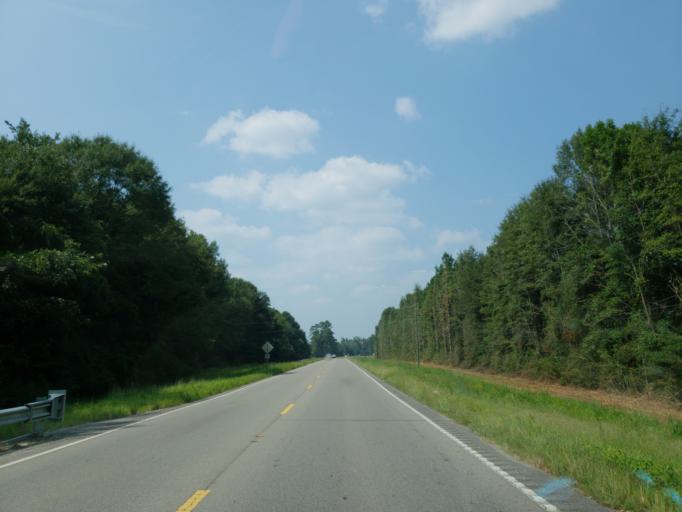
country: US
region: Mississippi
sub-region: Forrest County
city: Glendale
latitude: 31.4384
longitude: -89.2852
